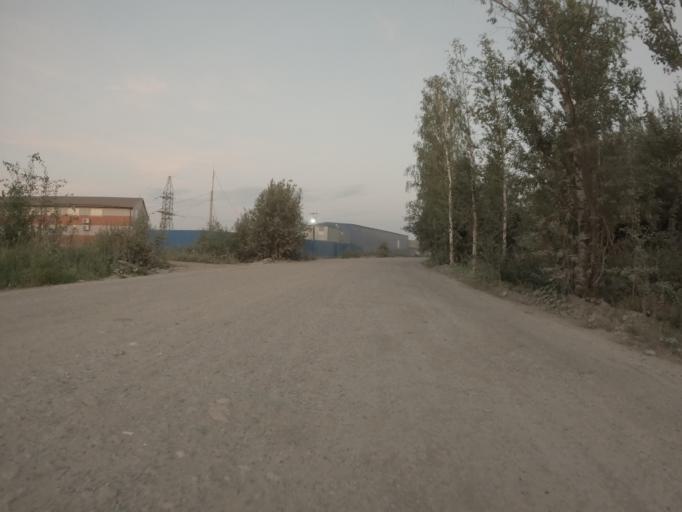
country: RU
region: Leningrad
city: Yanino Vtoroye
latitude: 59.9404
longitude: 30.6012
